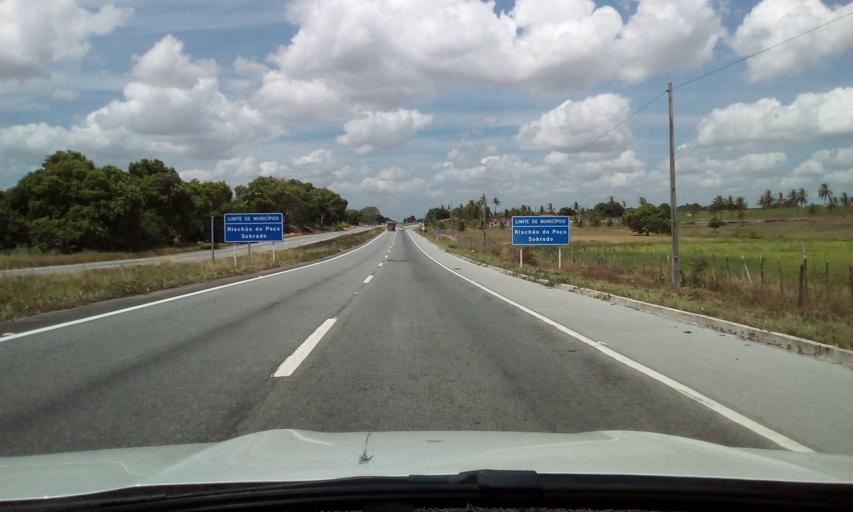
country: BR
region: Paraiba
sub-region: Pilar
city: Pilar
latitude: -7.1892
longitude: -35.2770
